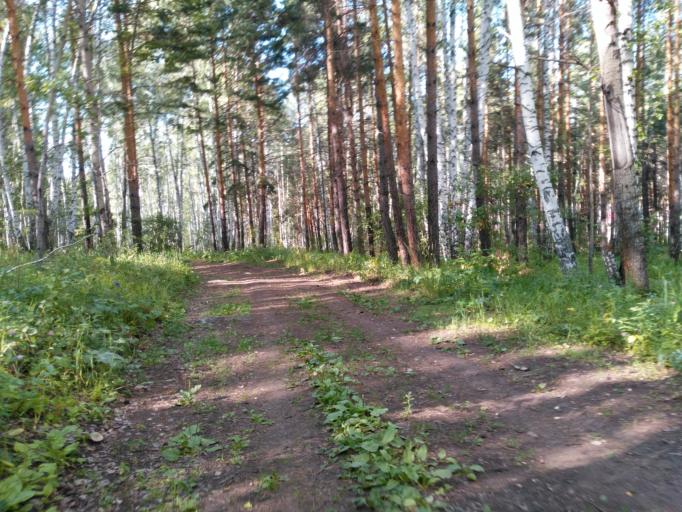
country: RU
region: Bashkortostan
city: Uchaly
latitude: 54.3319
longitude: 59.3576
